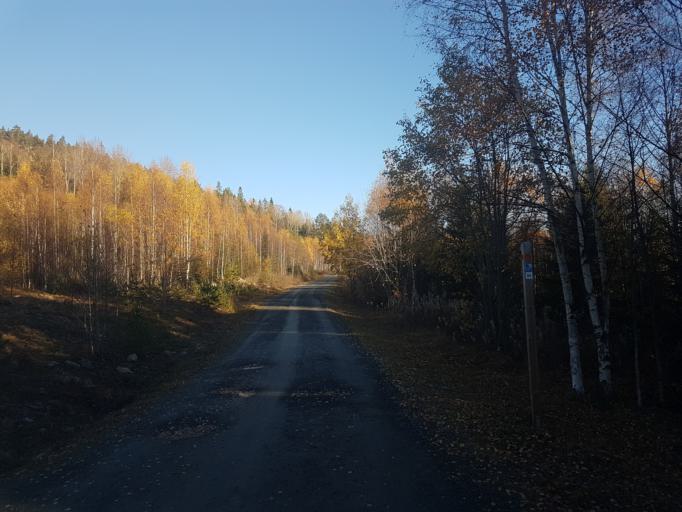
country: SE
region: Vaesternorrland
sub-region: OErnskoeldsviks Kommun
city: Bjasta
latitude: 63.0839
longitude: 18.4791
